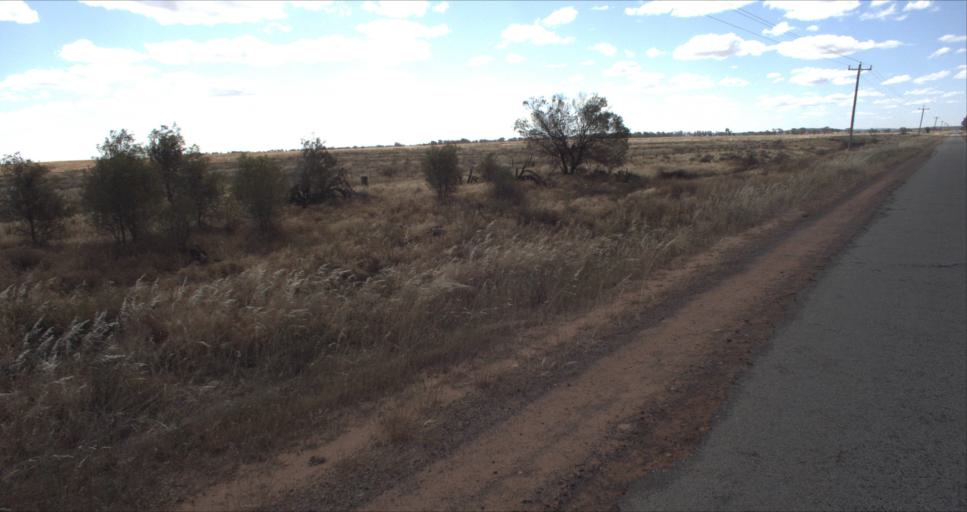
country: AU
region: New South Wales
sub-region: Leeton
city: Leeton
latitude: -34.4807
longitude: 146.2491
